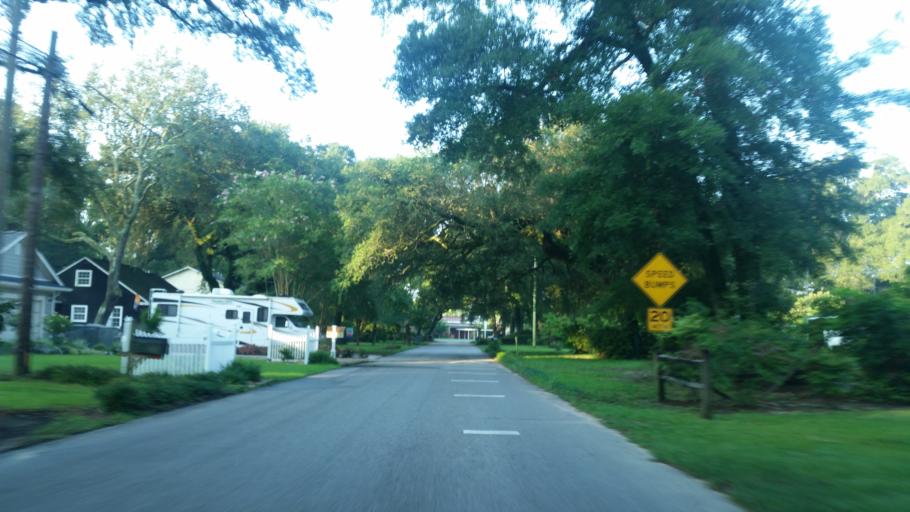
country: US
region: Florida
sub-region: Escambia County
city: Brent
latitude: 30.4860
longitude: -87.2404
